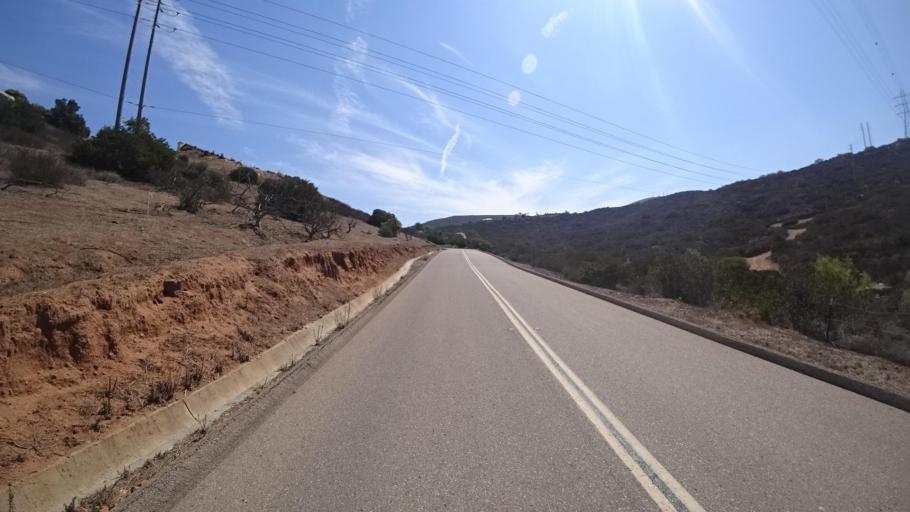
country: US
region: California
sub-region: San Diego County
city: Rancho San Diego
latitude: 32.7221
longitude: -116.9307
